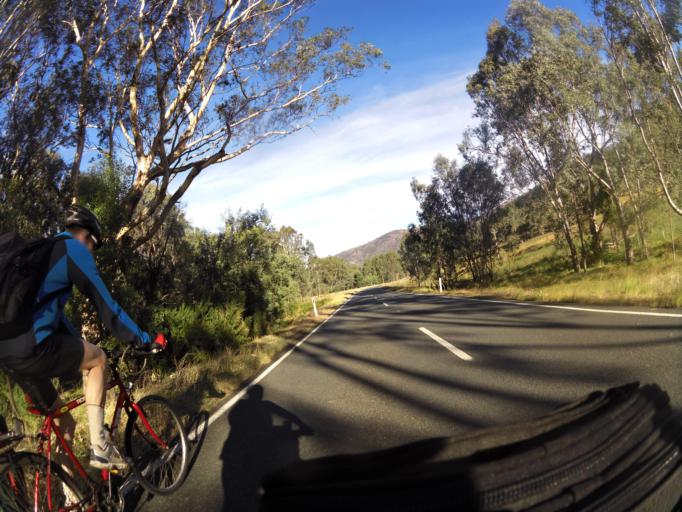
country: AU
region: New South Wales
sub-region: Greater Hume Shire
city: Holbrook
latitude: -35.9747
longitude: 147.8109
